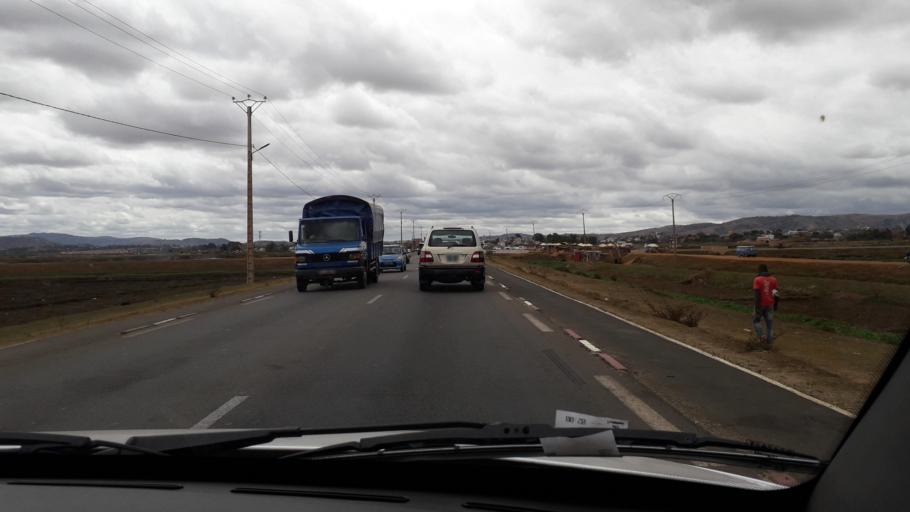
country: MG
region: Analamanga
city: Antananarivo
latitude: -18.8194
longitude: 47.5160
